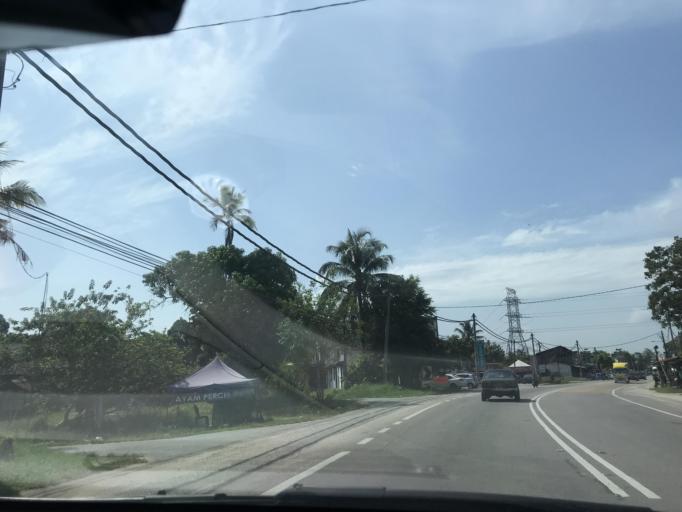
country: MY
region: Kelantan
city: Tumpat
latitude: 6.1493
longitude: 102.1613
